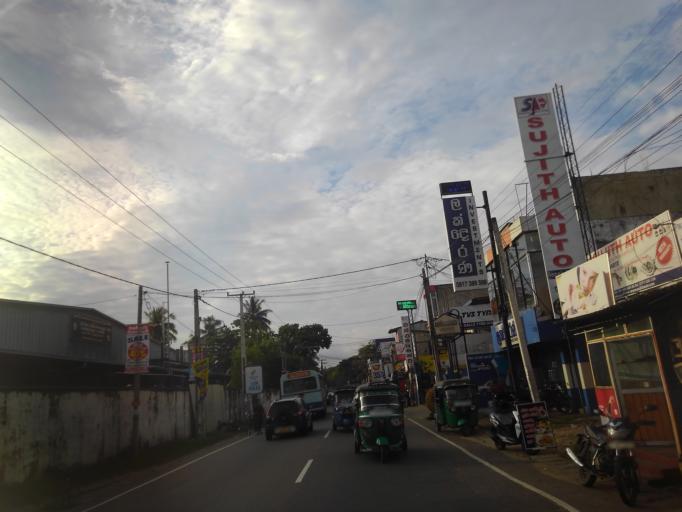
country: LK
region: Southern
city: Galle
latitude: 6.0361
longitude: 80.2308
